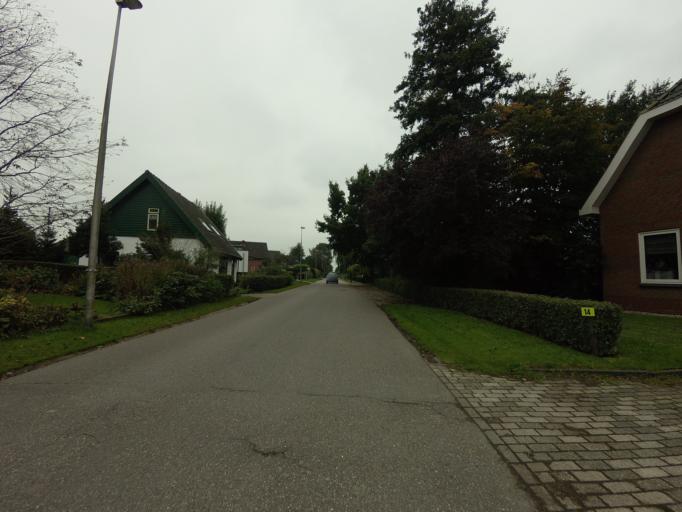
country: NL
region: South Holland
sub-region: Gemeente Nieuwkoop
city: Nieuwkoop
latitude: 52.1775
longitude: 4.7353
